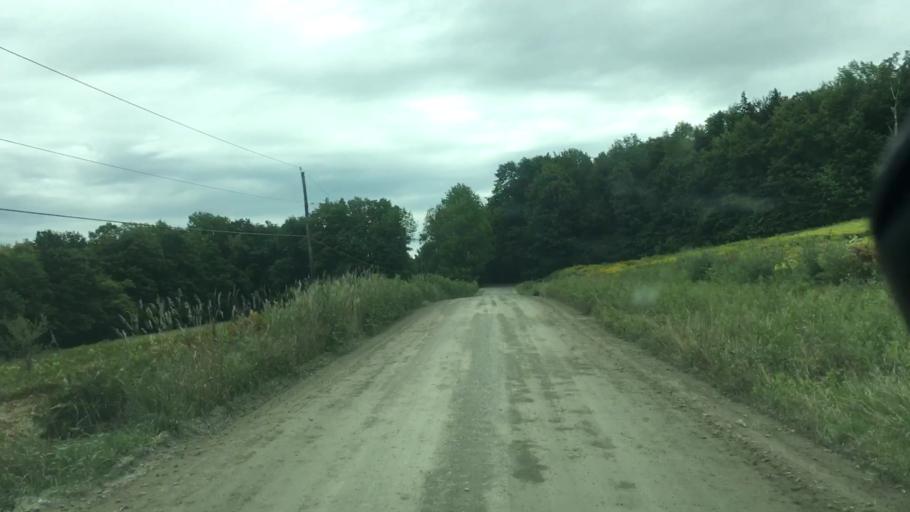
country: US
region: Vermont
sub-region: Windham County
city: Dover
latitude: 42.8561
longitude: -72.7796
